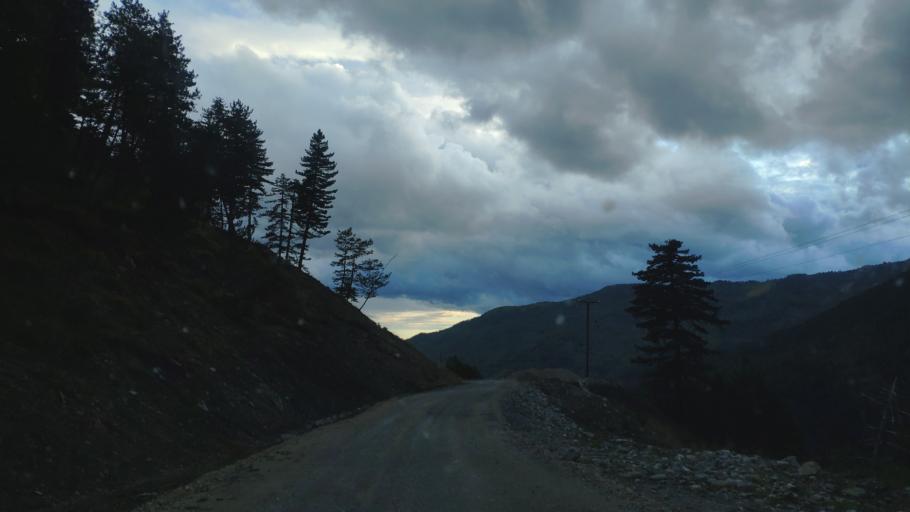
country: AL
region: Korce
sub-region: Rrethi i Kolonjes
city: Erseke
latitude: 40.2853
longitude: 20.8615
